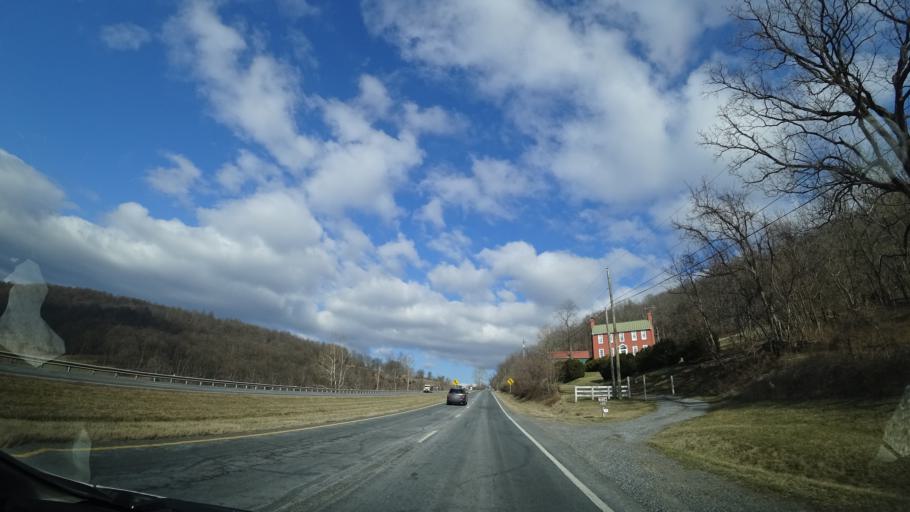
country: US
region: Virginia
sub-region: Warren County
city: Shenandoah Farms
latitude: 39.0094
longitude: -77.9549
